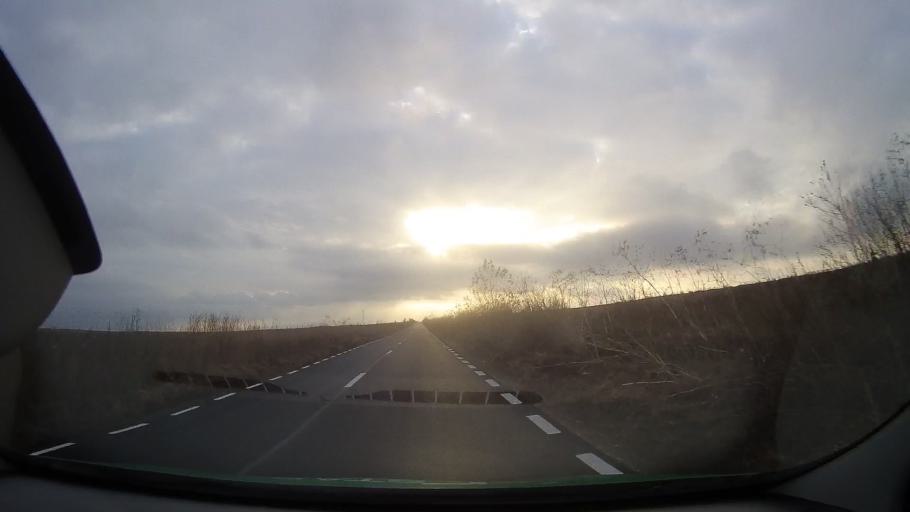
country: RO
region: Constanta
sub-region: Comuna Deleni
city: Deleni
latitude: 44.0760
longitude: 27.9914
